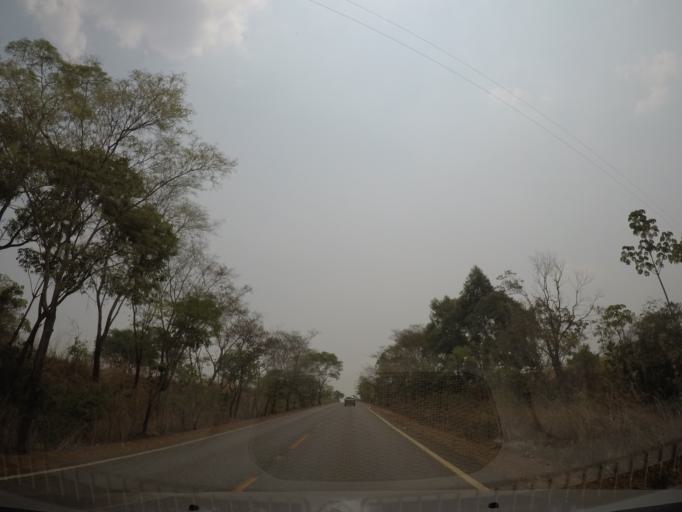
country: BR
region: Goias
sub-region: Pirenopolis
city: Pirenopolis
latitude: -15.8958
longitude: -48.8795
